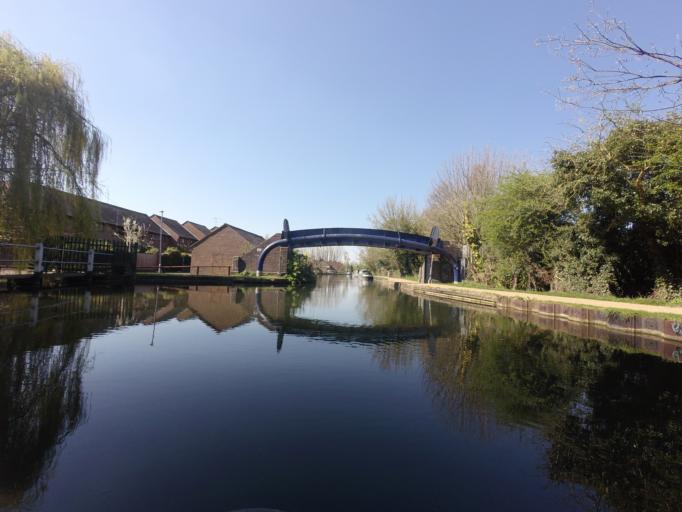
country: GB
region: England
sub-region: Hertfordshire
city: Kings Langley
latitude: 51.7151
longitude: -0.4452
